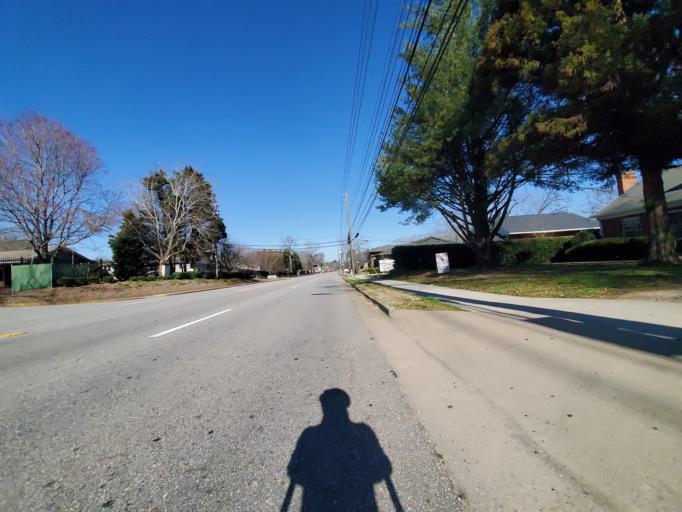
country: US
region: Georgia
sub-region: Clarke County
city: Country Club Estates
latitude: 33.9661
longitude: -83.4049
